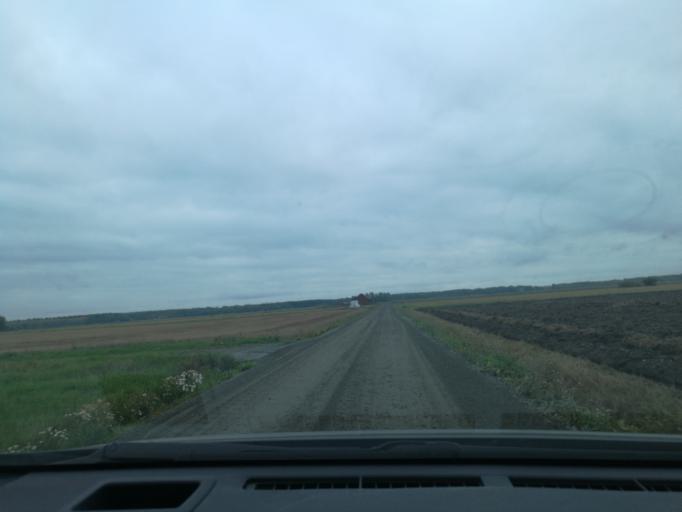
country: SE
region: Vaestmanland
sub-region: Vasteras
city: Tillberga
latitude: 59.7721
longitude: 16.6501
